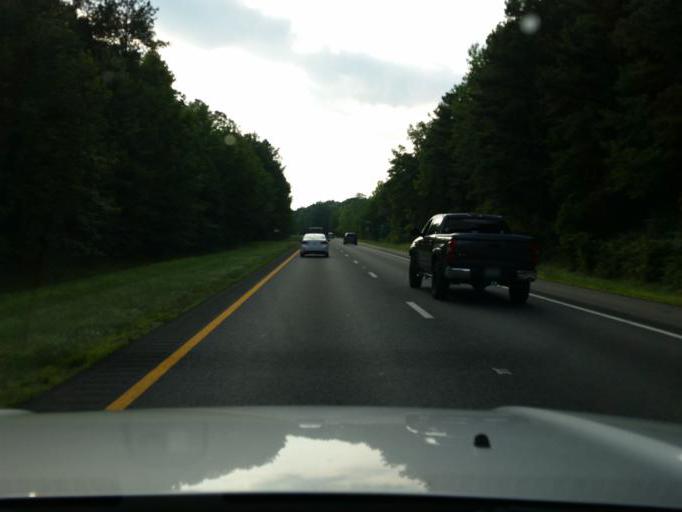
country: US
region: Virginia
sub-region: New Kent County
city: New Kent
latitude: 37.4757
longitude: -76.9102
